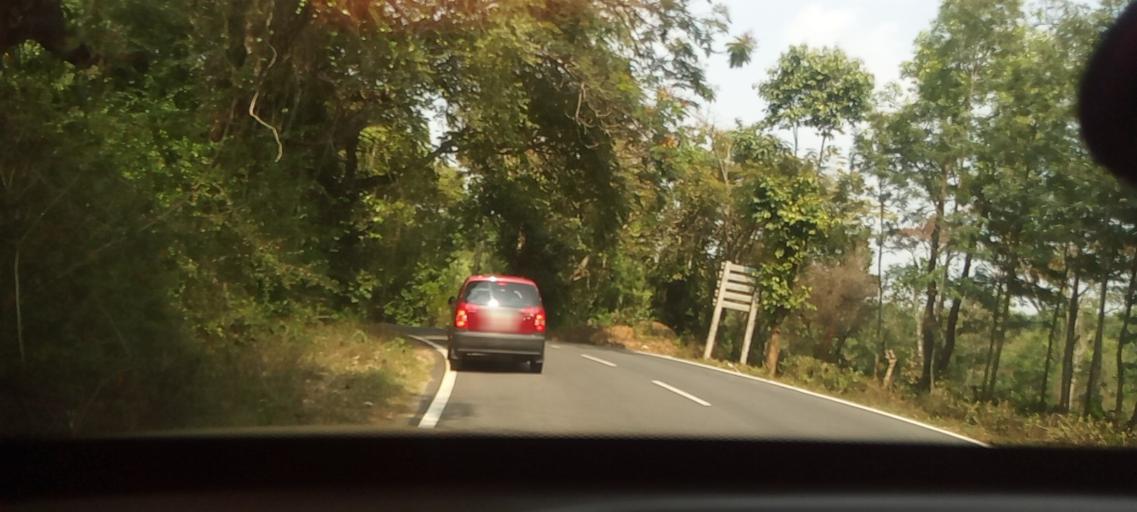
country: IN
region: Karnataka
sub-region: Chikmagalur
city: Chikmagalur
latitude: 13.2606
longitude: 75.6743
